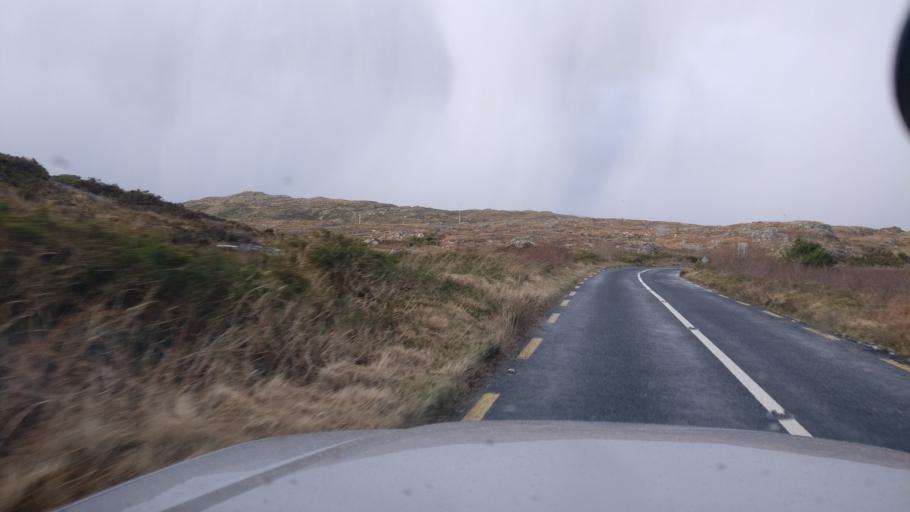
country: IE
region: Connaught
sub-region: County Galway
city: Clifden
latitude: 53.4172
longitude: -9.7782
